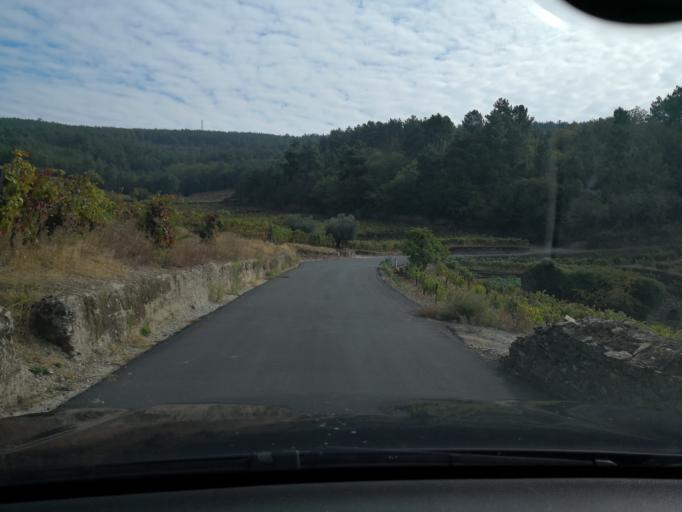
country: PT
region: Vila Real
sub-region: Sabrosa
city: Vilela
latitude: 41.2152
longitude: -7.6839
